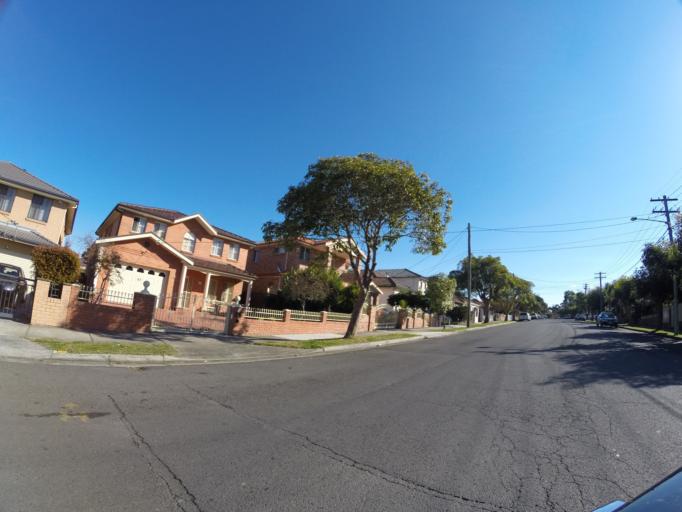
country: AU
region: New South Wales
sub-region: Auburn
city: Lidcombe
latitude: -33.8593
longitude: 151.0495
